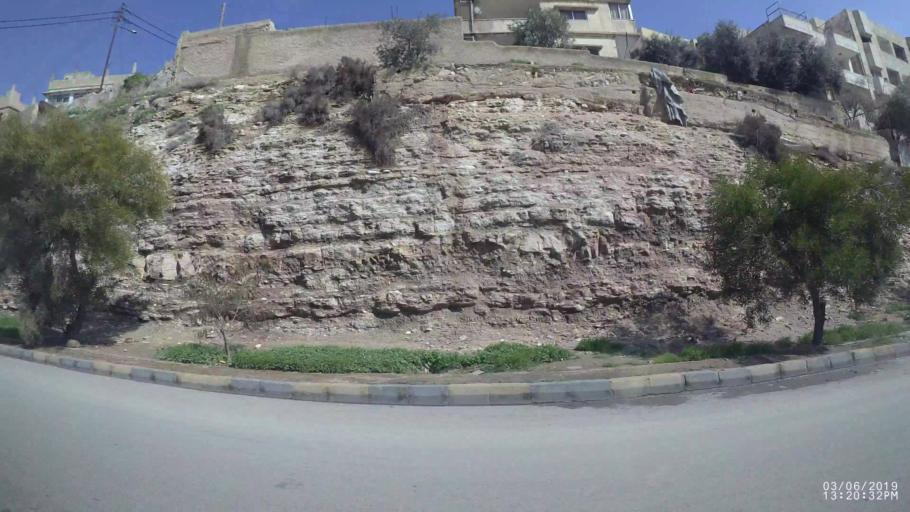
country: JO
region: Zarqa
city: Zarqa
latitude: 32.0484
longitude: 36.0922
